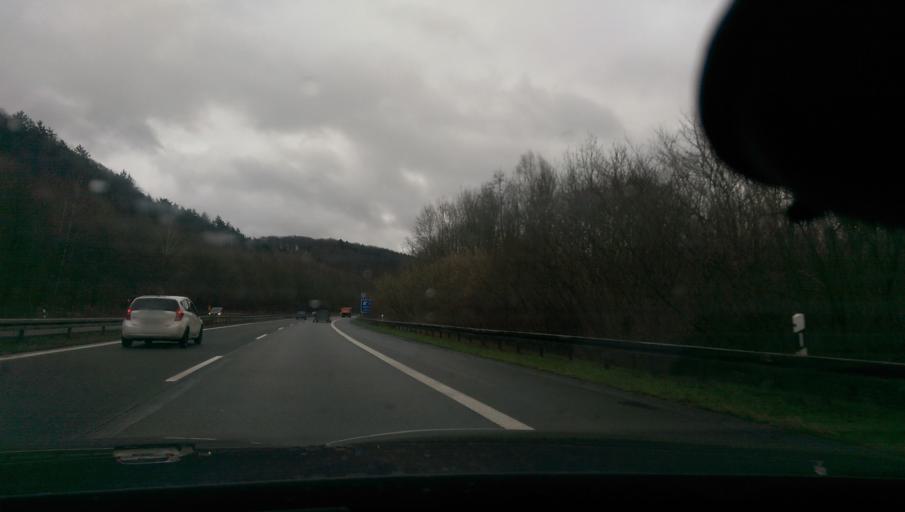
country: DE
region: North Rhine-Westphalia
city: Wickede
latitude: 51.4692
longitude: 7.9486
